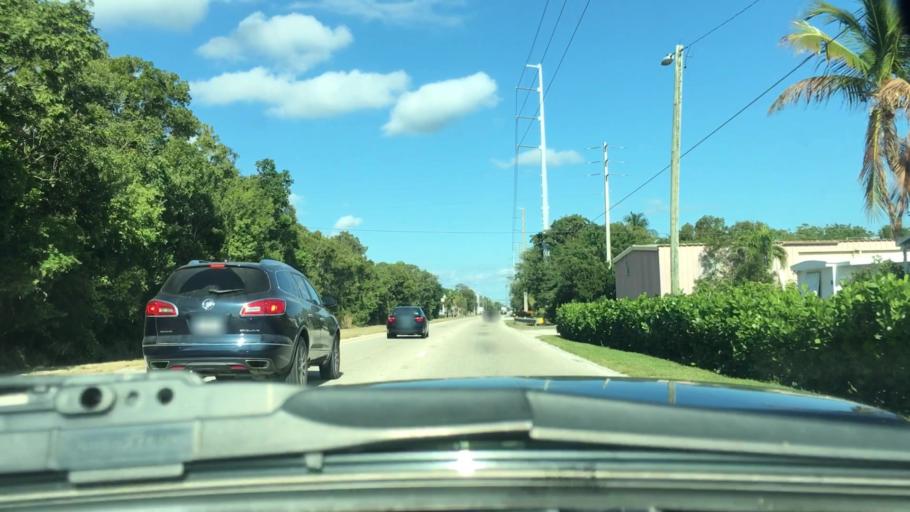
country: US
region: Florida
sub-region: Monroe County
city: Key Largo
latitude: 25.0721
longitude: -80.4646
